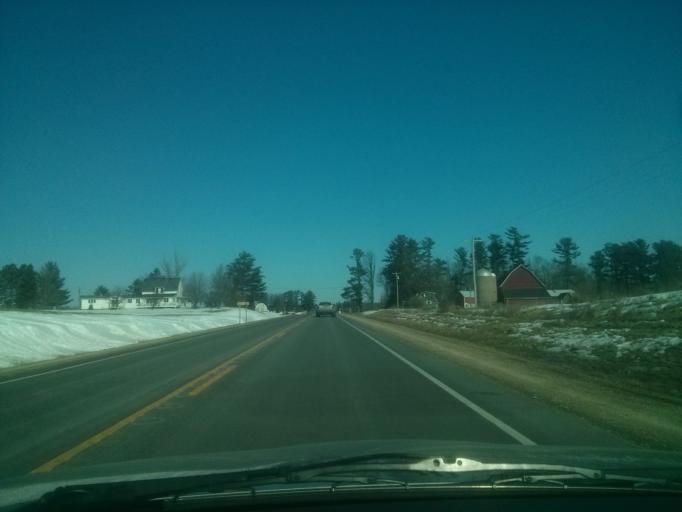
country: US
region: Wisconsin
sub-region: Polk County
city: Clear Lake
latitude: 45.1813
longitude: -92.2832
